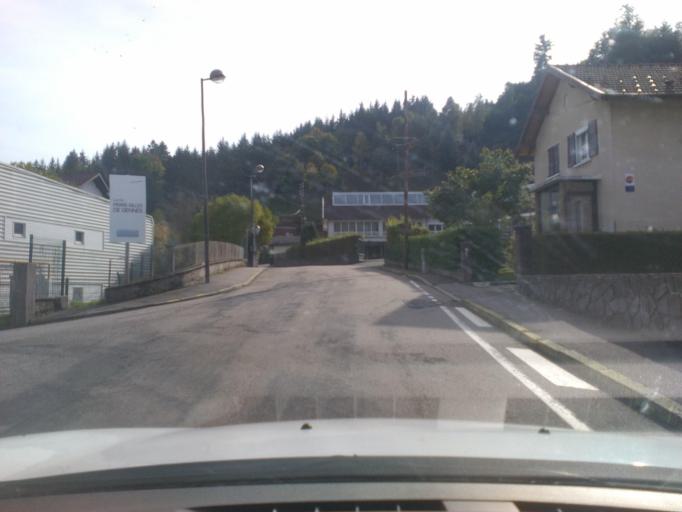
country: FR
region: Lorraine
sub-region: Departement des Vosges
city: Gerardmer
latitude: 48.0654
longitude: 6.8702
